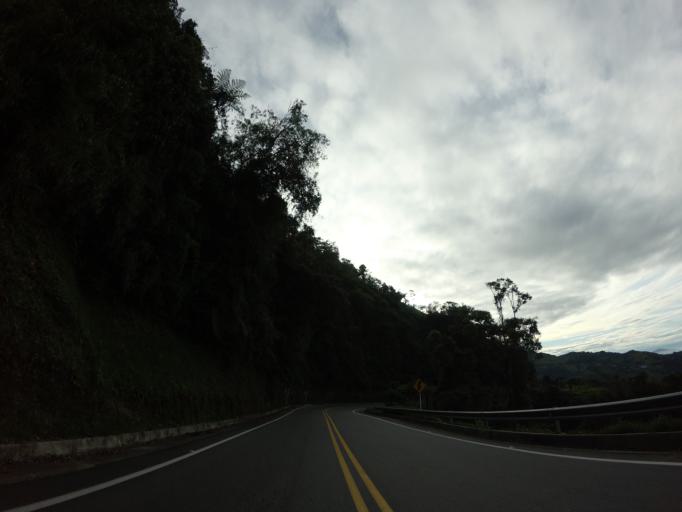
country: CO
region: Tolima
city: Herveo
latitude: 5.1056
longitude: -75.2558
